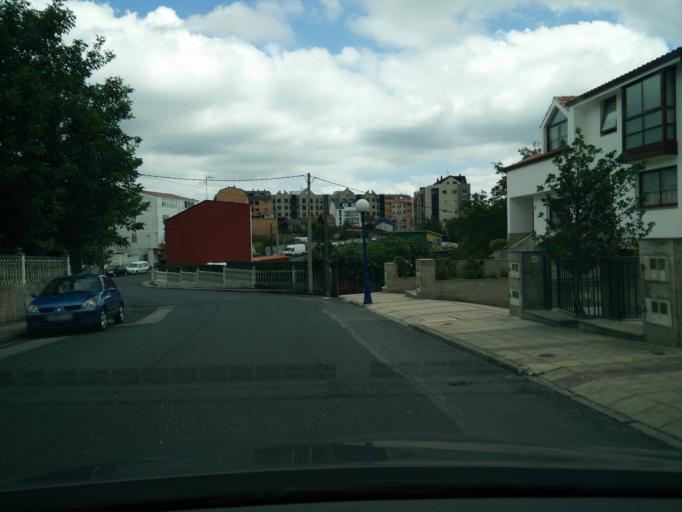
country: ES
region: Galicia
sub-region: Provincia da Coruna
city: Culleredo
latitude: 43.3128
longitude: -8.3858
